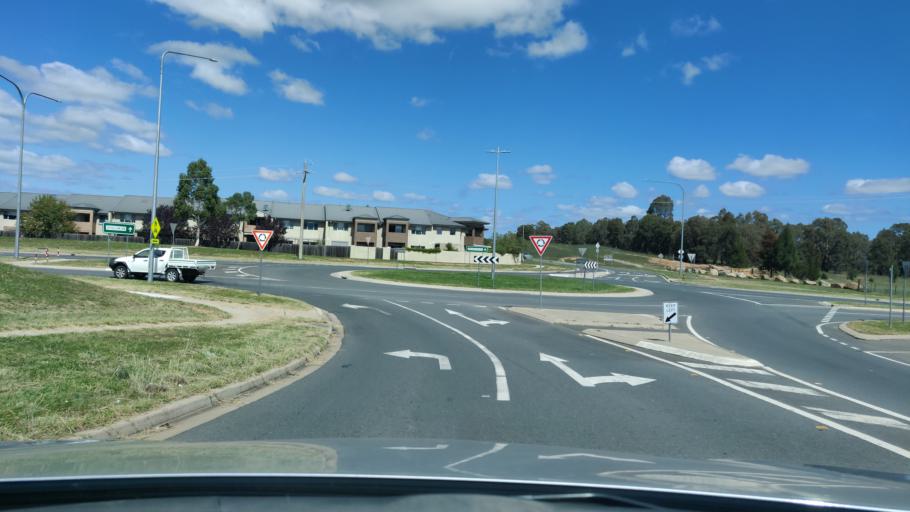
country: AU
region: Australian Capital Territory
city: Macarthur
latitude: -35.4245
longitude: 149.0703
